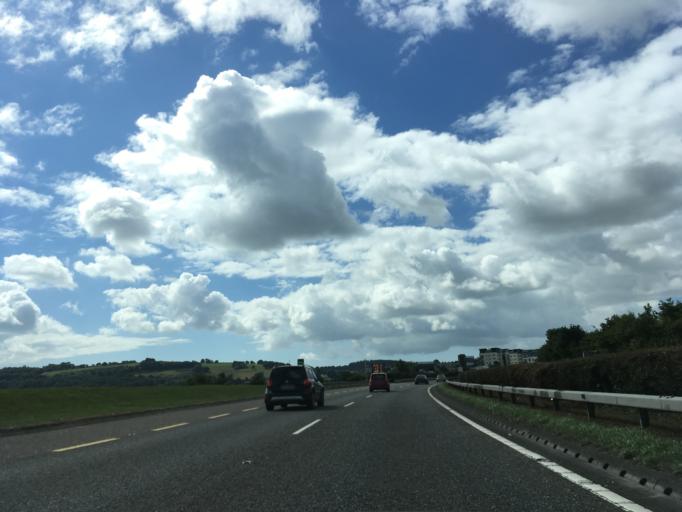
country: IE
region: Munster
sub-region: County Cork
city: Passage West
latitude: 51.8897
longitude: -8.3904
